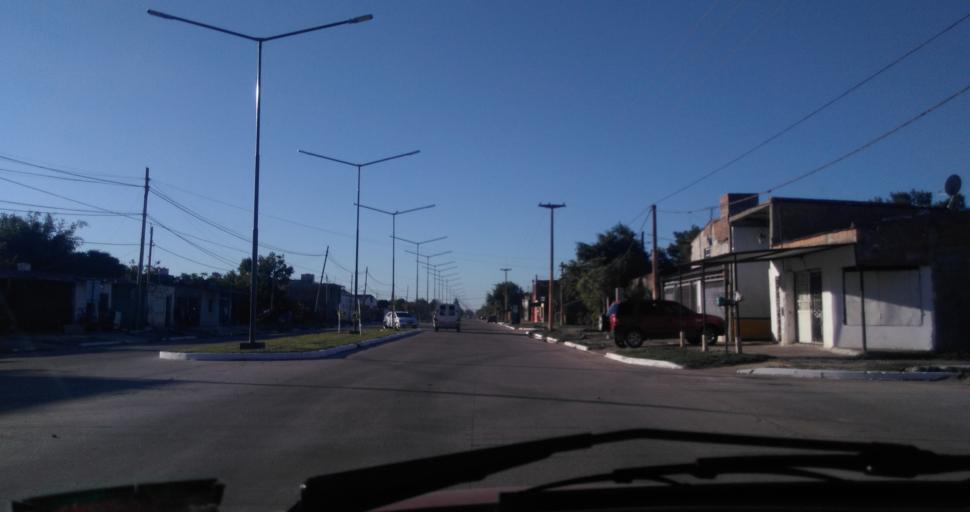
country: AR
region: Chaco
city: Resistencia
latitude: -27.4813
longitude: -58.9812
